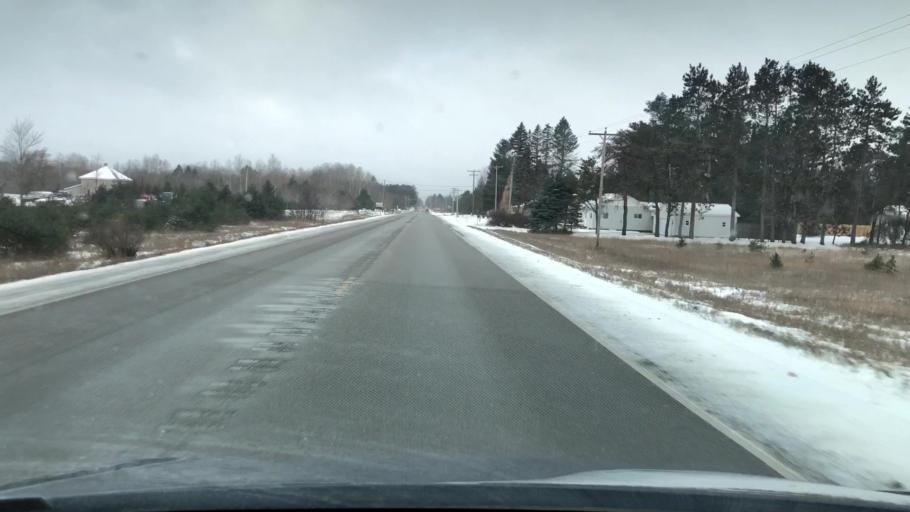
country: US
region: Michigan
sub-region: Wexford County
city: Cadillac
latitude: 44.2812
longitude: -85.4509
